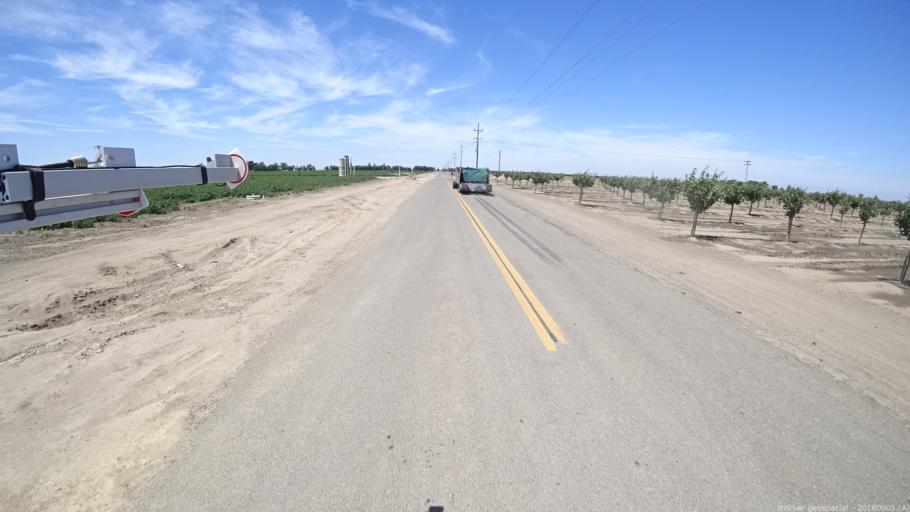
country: US
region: California
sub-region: Merced County
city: Dos Palos
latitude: 37.0901
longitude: -120.4734
